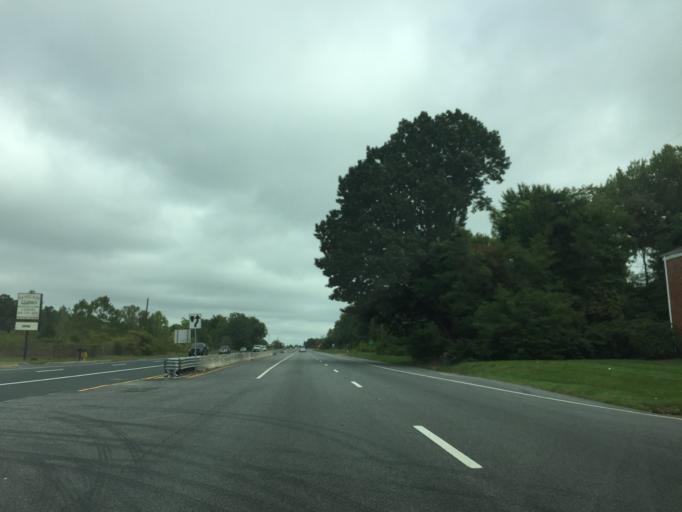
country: US
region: Maryland
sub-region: Baltimore County
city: Rossville
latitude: 39.3447
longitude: -76.4653
